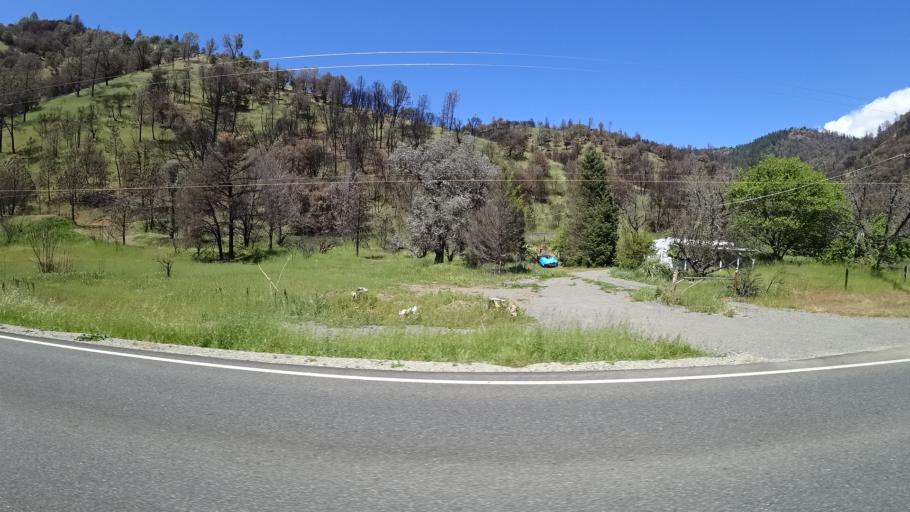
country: US
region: California
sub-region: Trinity County
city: Weaverville
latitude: 40.7685
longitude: -123.0878
